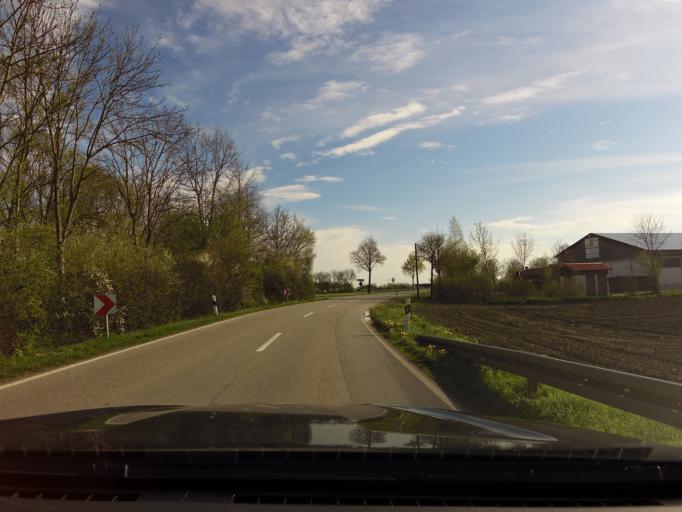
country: DE
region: Bavaria
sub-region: Upper Bavaria
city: Hallbergmoos
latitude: 48.3328
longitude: 11.7558
